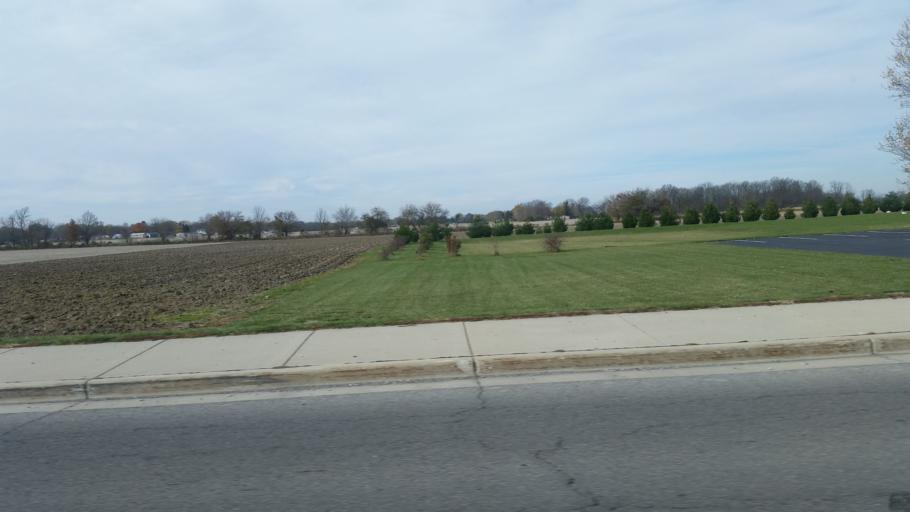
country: US
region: Indiana
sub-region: Howard County
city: Indian Heights
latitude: 40.4461
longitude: -86.1652
